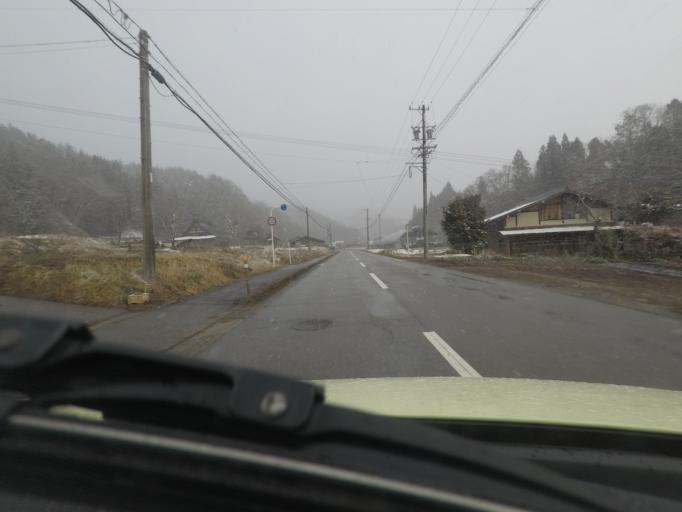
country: JP
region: Gifu
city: Takayama
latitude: 36.1427
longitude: 137.3046
